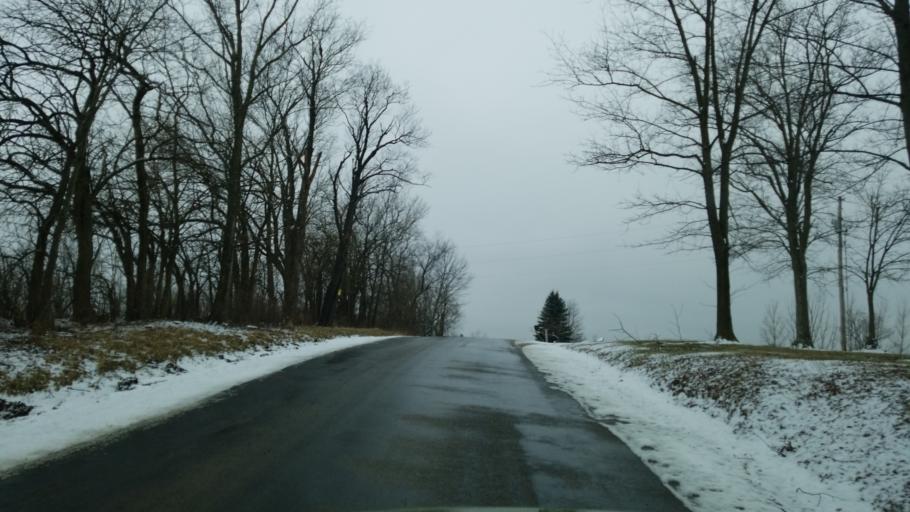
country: US
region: Pennsylvania
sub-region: Jefferson County
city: Sykesville
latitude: 41.0850
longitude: -78.8422
